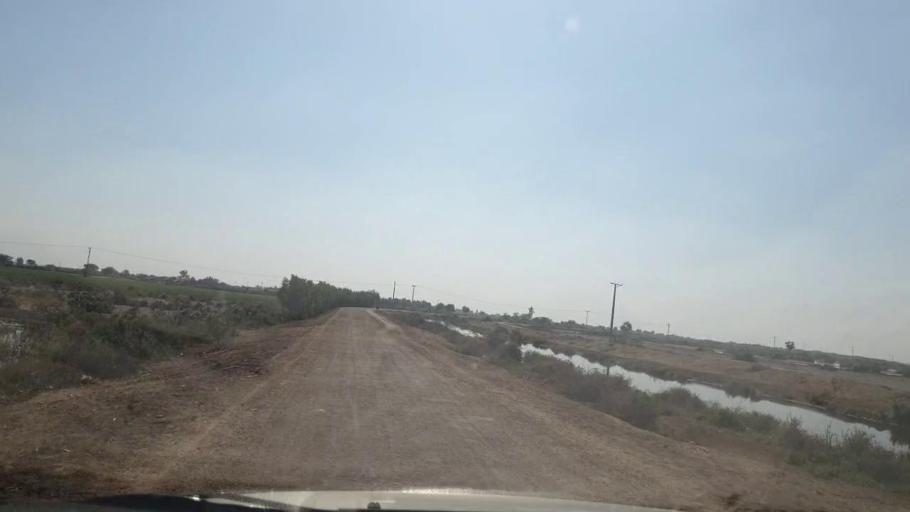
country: PK
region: Sindh
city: Mirpur Khas
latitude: 25.5133
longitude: 69.0853
